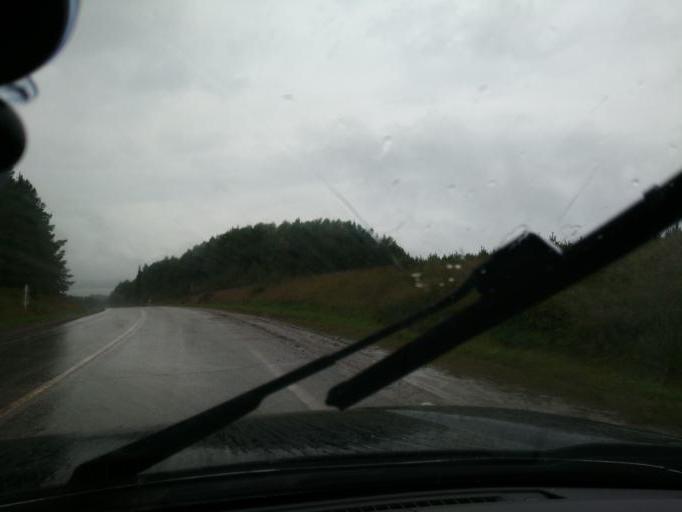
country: RU
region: Perm
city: Osa
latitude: 57.3241
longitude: 55.6119
